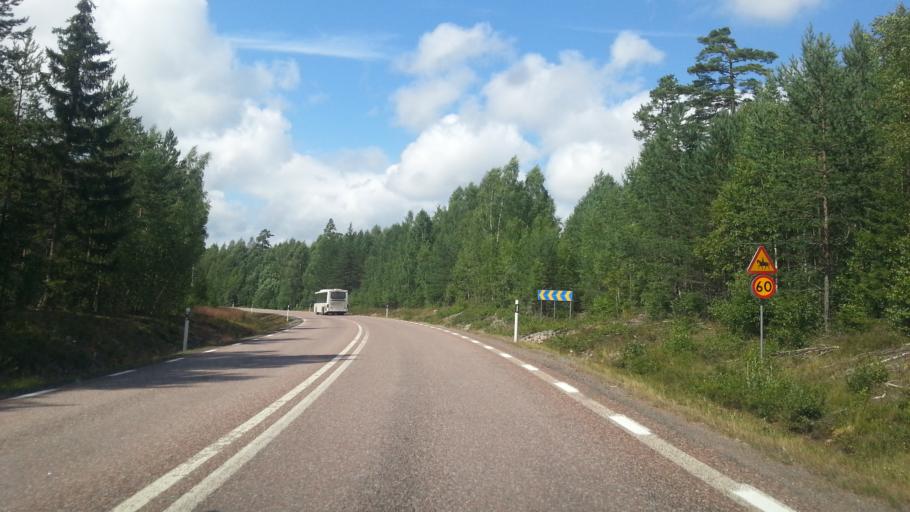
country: SE
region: Dalarna
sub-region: Faluns Kommun
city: Falun
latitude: 60.6133
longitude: 15.7291
